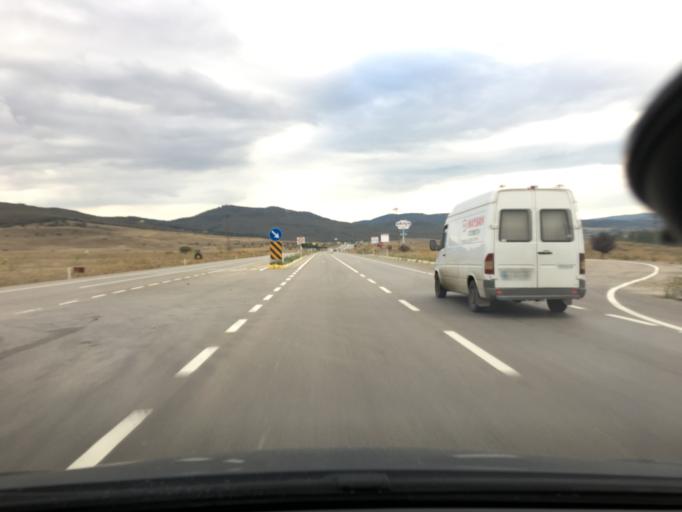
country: TR
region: Afyonkarahisar
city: Sincanli
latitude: 38.7222
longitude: 30.3366
